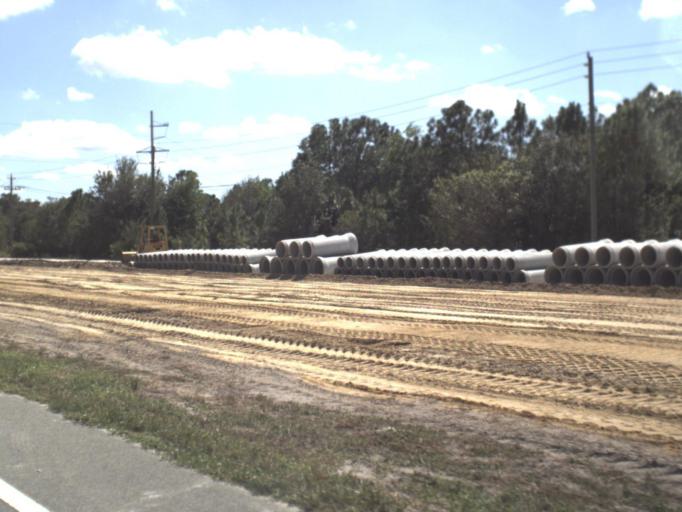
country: US
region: Florida
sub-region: Collier County
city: Lely Resort
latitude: 26.0541
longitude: -81.6847
